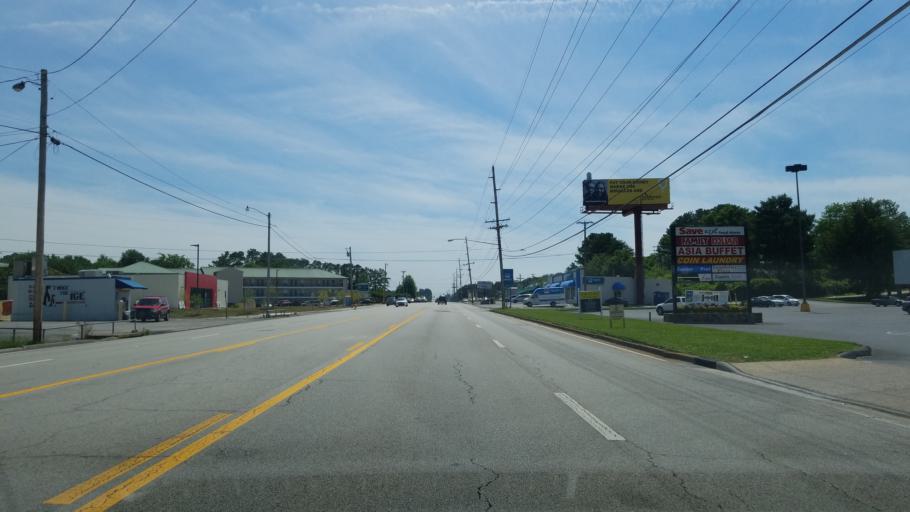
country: US
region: Tennessee
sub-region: Hamilton County
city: East Brainerd
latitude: 35.0429
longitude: -85.1657
